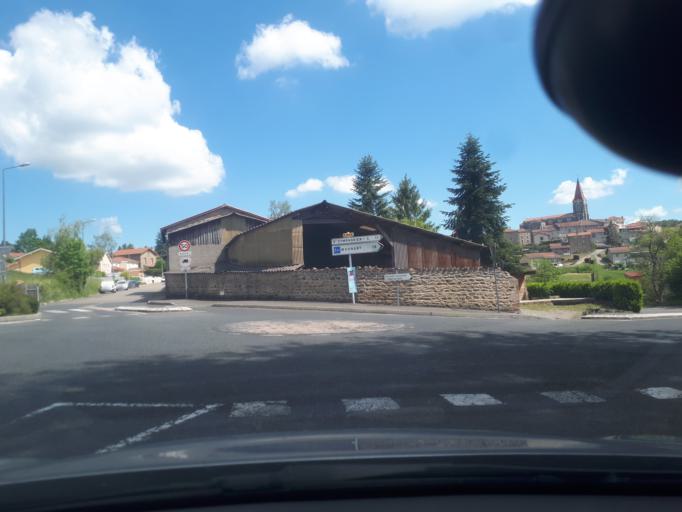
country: FR
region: Rhone-Alpes
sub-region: Departement du Rhone
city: Saint-Martin-en-Haut
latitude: 45.6637
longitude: 4.5572
